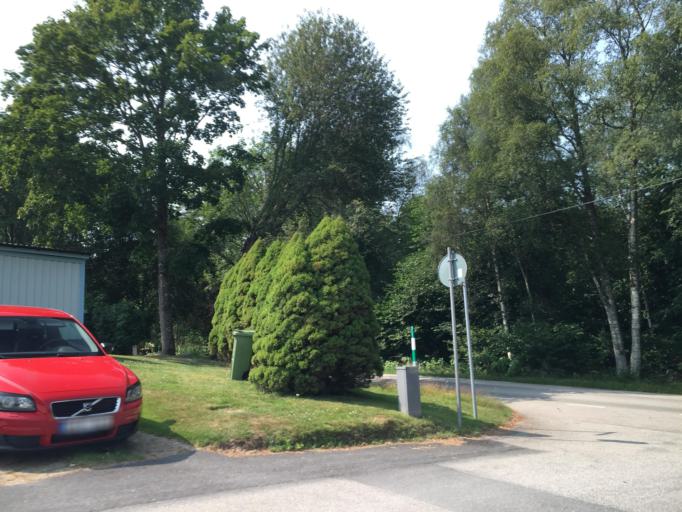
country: SE
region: Vaestra Goetaland
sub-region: Lilla Edets Kommun
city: Lilla Edet
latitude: 58.1823
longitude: 12.1121
